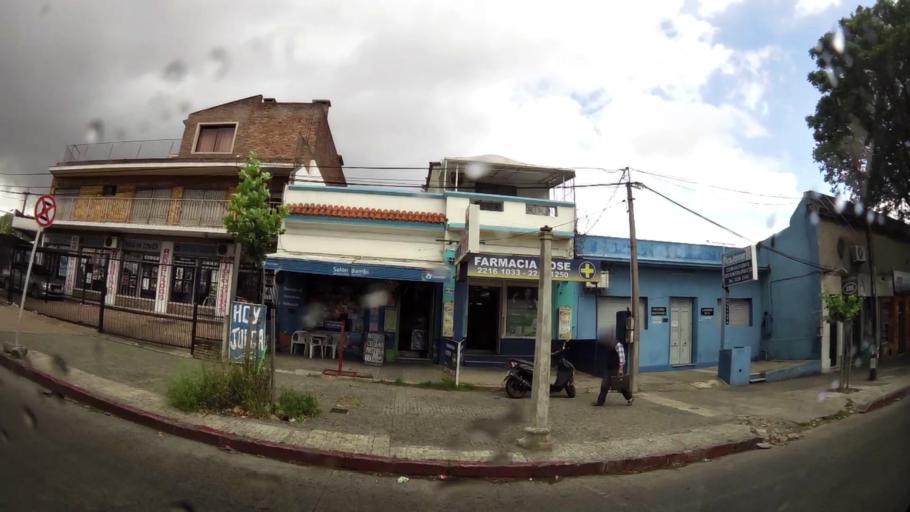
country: UY
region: Montevideo
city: Montevideo
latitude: -34.8574
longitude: -56.1757
